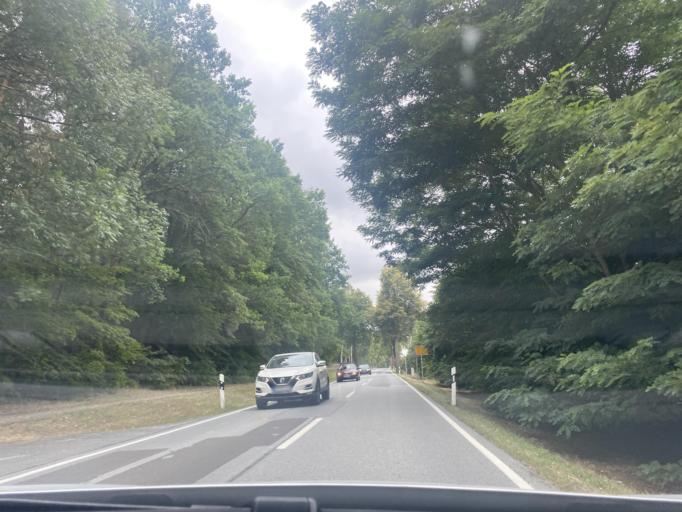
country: DE
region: Saxony
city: Guttau
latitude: 51.2685
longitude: 14.6105
